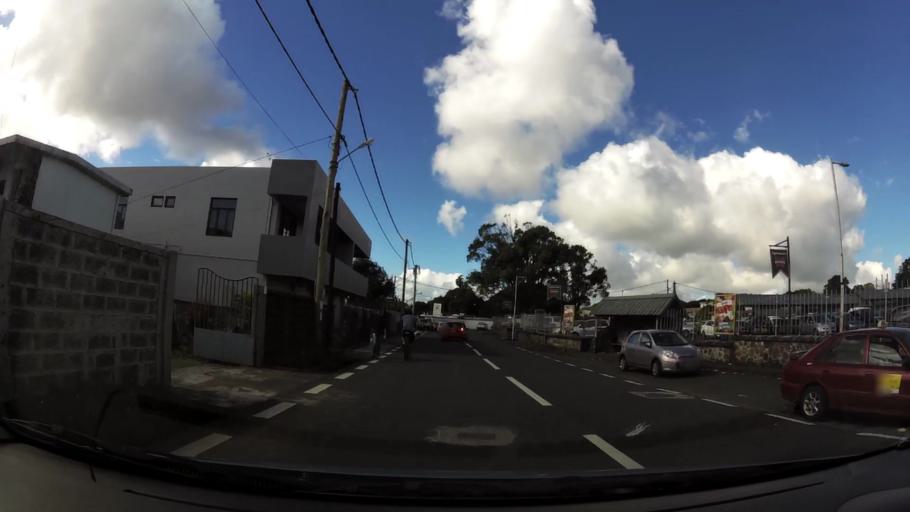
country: MU
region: Plaines Wilhems
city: Curepipe
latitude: -20.3272
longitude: 57.5281
